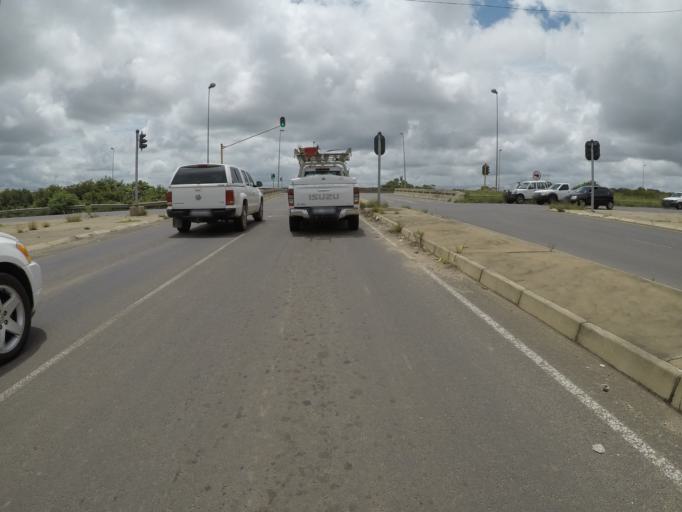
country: ZA
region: KwaZulu-Natal
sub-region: uThungulu District Municipality
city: Empangeni
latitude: -28.7757
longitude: 31.9585
